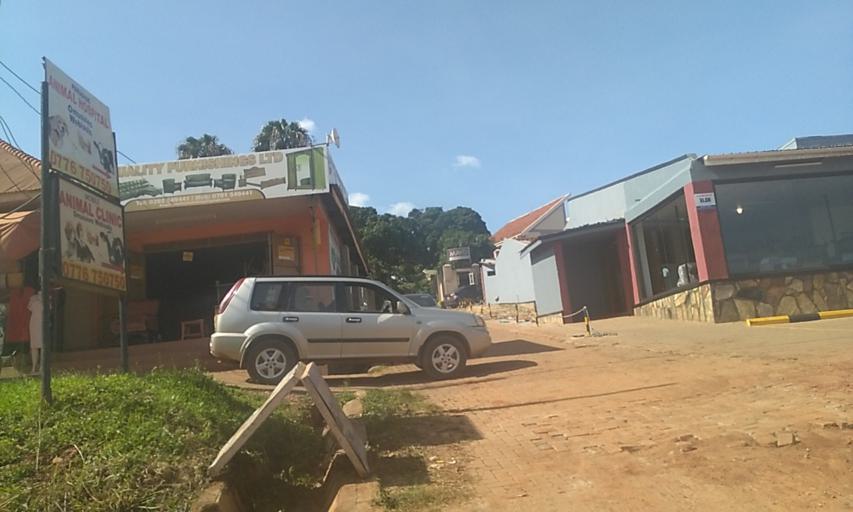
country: UG
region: Central Region
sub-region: Wakiso District
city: Kireka
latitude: 0.3527
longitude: 32.6090
